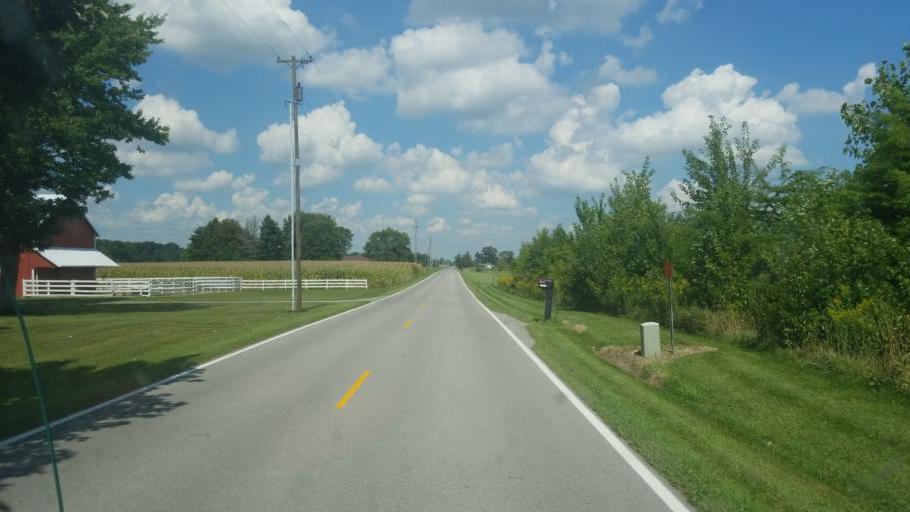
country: US
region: Ohio
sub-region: Hancock County
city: Arlington
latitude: 40.8826
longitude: -83.7271
